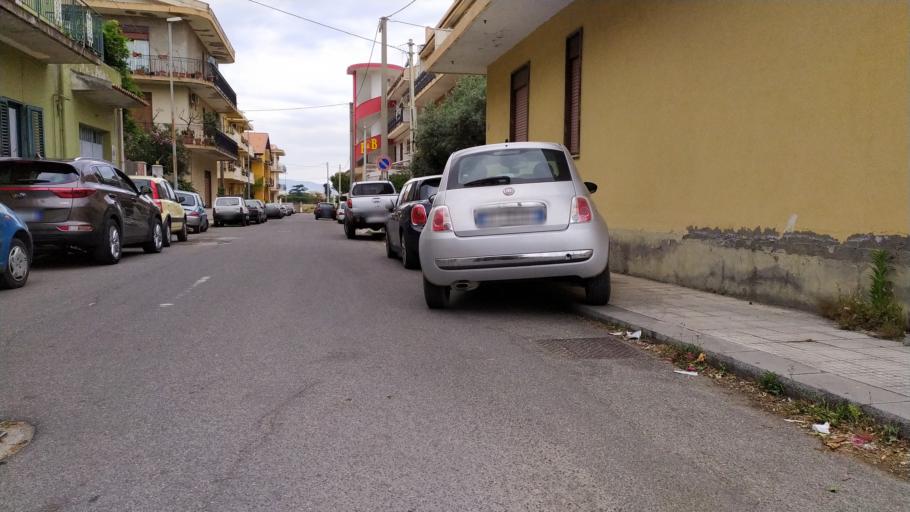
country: IT
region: Sicily
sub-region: Messina
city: Meri
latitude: 38.1874
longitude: 15.2537
